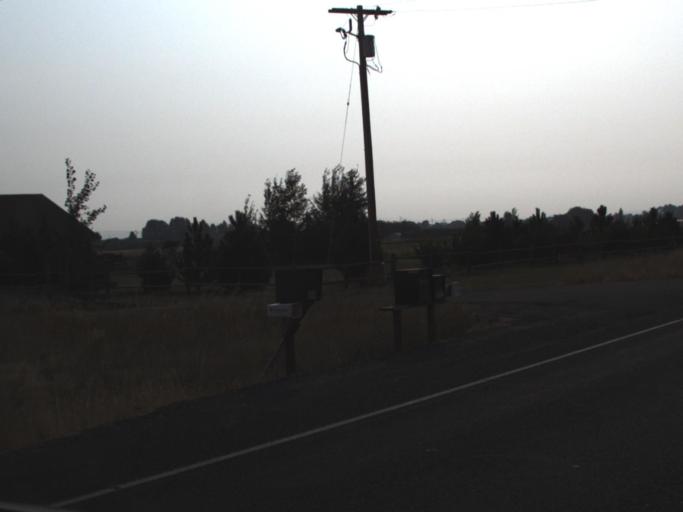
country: US
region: Washington
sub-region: Kittitas County
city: Ellensburg
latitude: 47.0313
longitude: -120.6060
